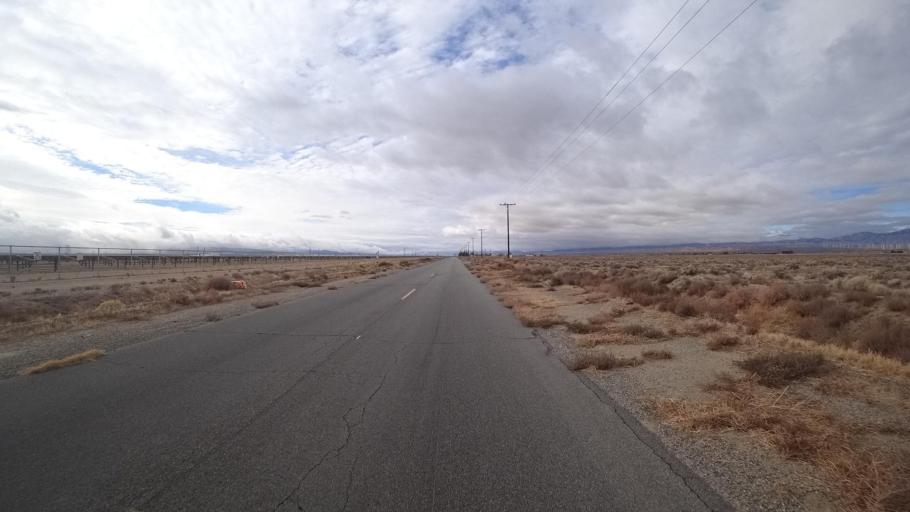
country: US
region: California
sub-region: Los Angeles County
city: Green Valley
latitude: 34.8192
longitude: -118.3869
